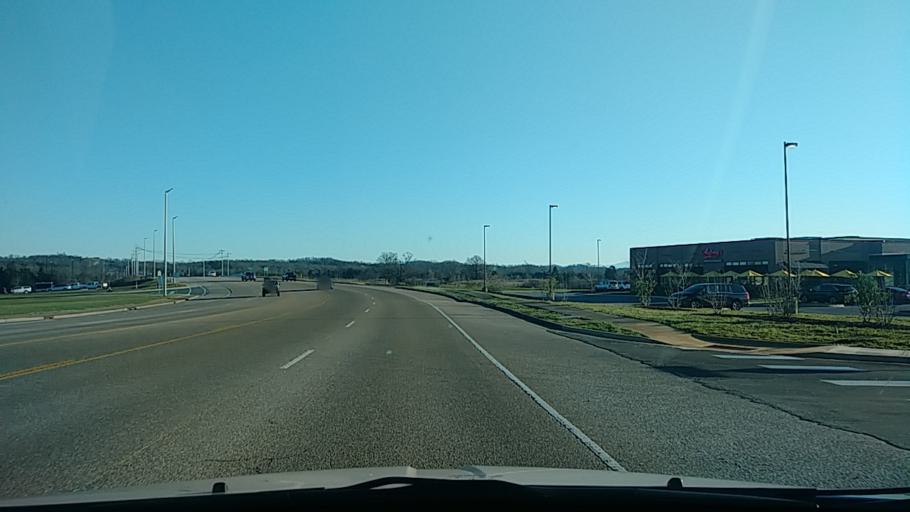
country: US
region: Tennessee
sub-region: Hamblen County
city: Morristown
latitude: 36.1905
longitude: -83.3592
